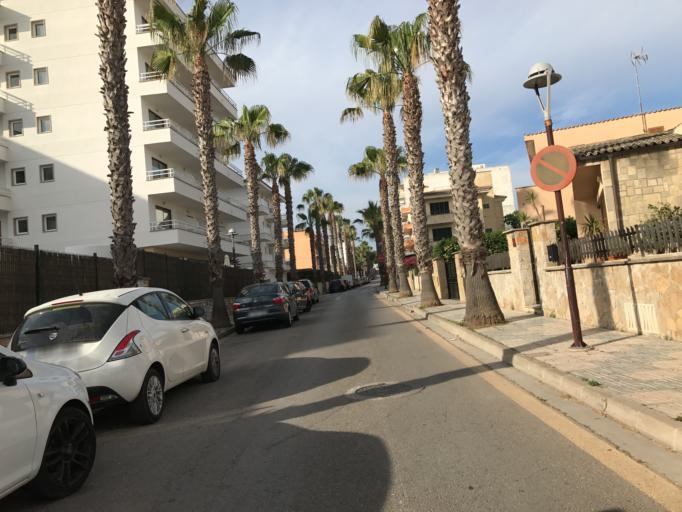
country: ES
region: Balearic Islands
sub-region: Illes Balears
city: Port d'Alcudia
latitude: 39.7672
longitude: 3.1502
